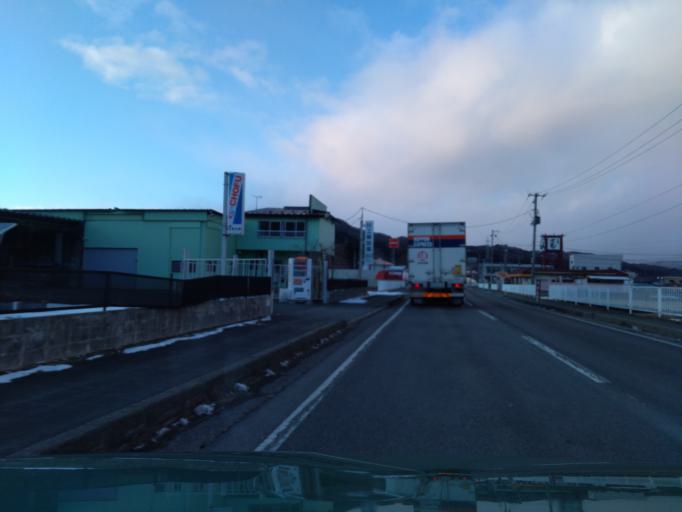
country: JP
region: Iwate
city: Shizukuishi
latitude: 39.6987
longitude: 141.0628
